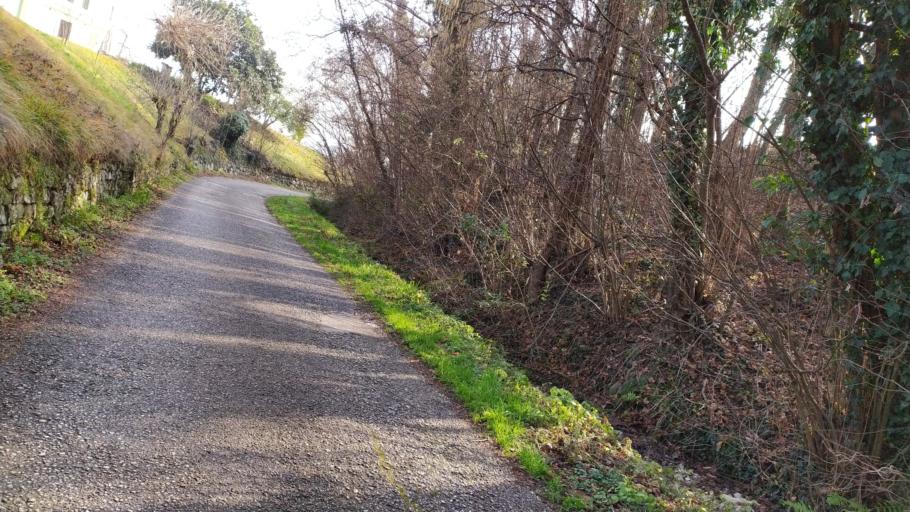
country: IT
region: Veneto
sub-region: Provincia di Treviso
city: Colle Umberto
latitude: 45.9423
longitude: 12.3482
